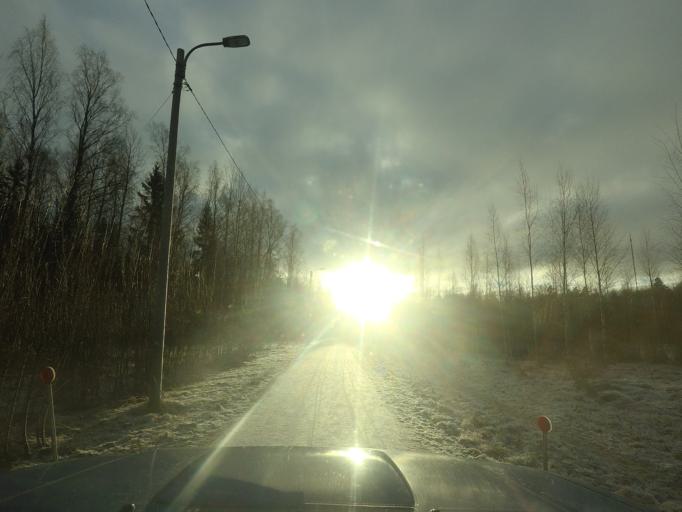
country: FI
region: Uusimaa
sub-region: Helsinki
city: Espoo
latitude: 60.1895
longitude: 24.6558
